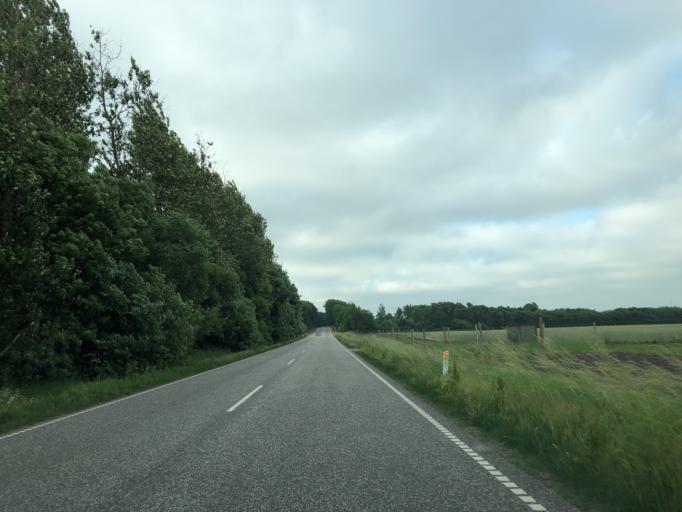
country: DK
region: South Denmark
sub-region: Vejle Kommune
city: Give
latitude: 55.8707
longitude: 9.2379
